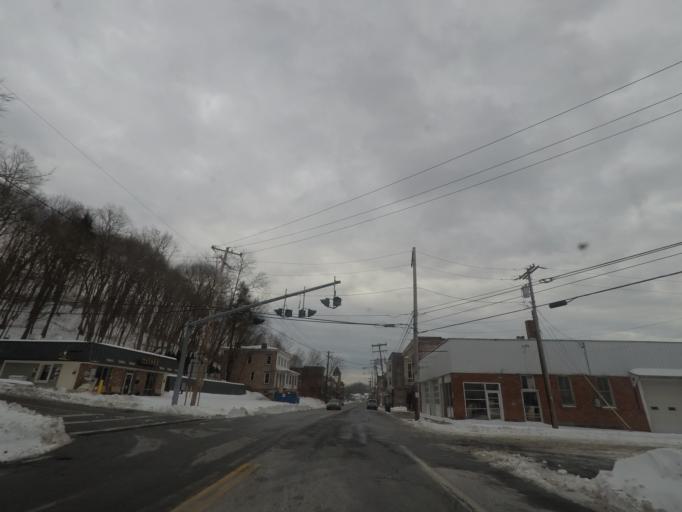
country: US
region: New York
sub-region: Rensselaer County
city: Castleton-on-Hudson
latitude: 42.5316
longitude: -73.7563
